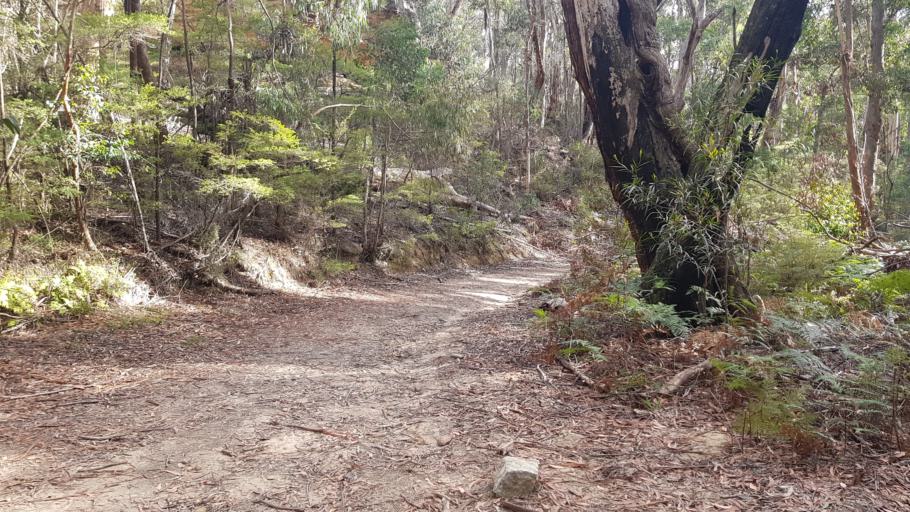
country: AU
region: New South Wales
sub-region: Lithgow
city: Lithgow
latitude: -33.2357
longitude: 150.2314
